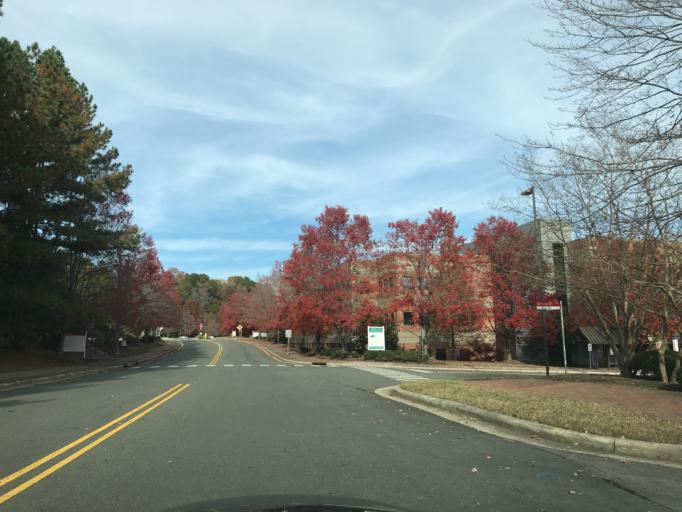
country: US
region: North Carolina
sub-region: Wake County
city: West Raleigh
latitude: 35.7714
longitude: -78.6812
